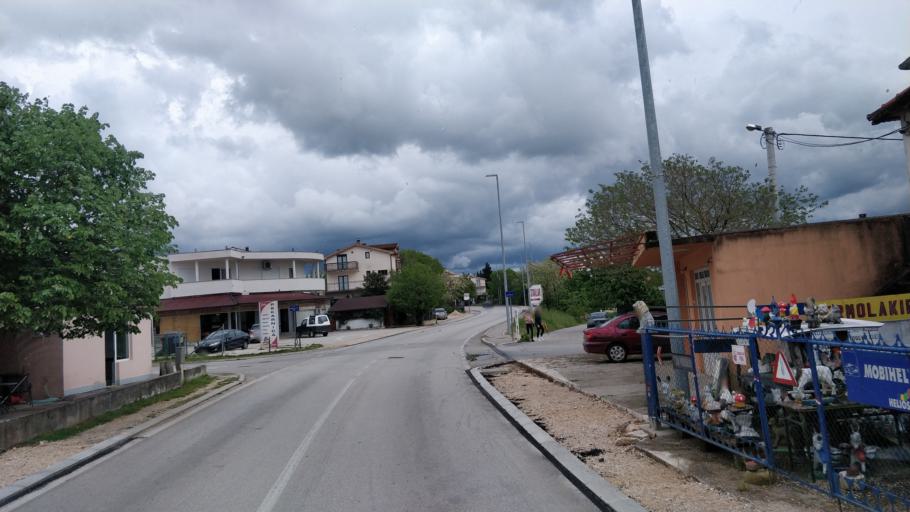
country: BA
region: Federation of Bosnia and Herzegovina
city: Ljubuski
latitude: 43.1894
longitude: 17.5367
